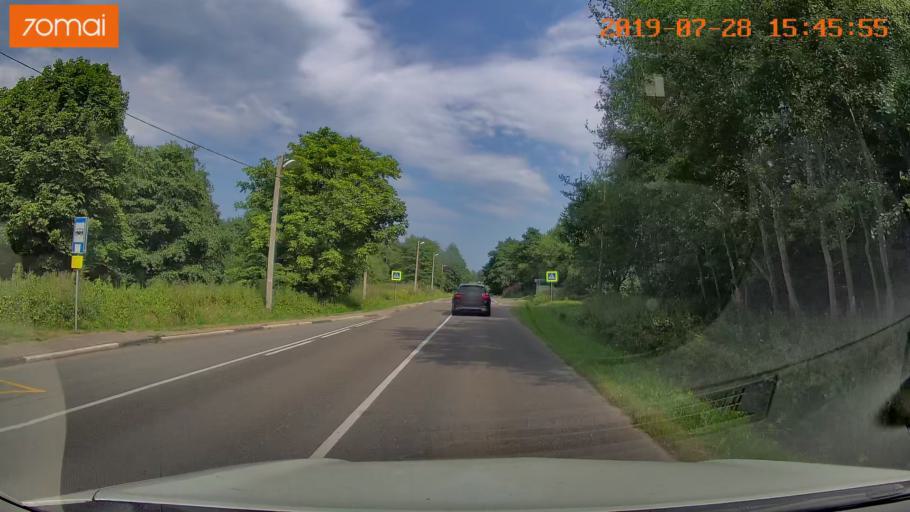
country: RU
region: Kaliningrad
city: Otradnoye
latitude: 54.9423
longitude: 20.0473
